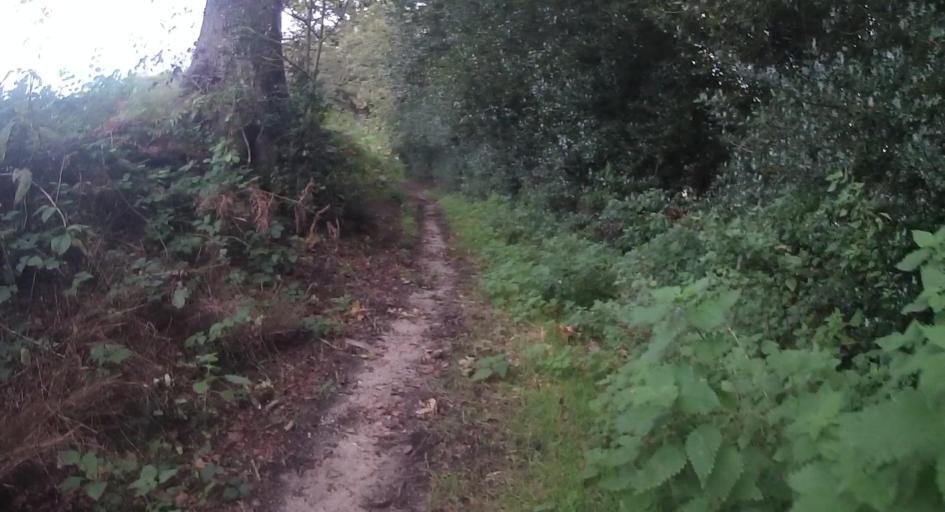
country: GB
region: England
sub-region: Hampshire
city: Hook
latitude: 51.3164
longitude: -0.9280
